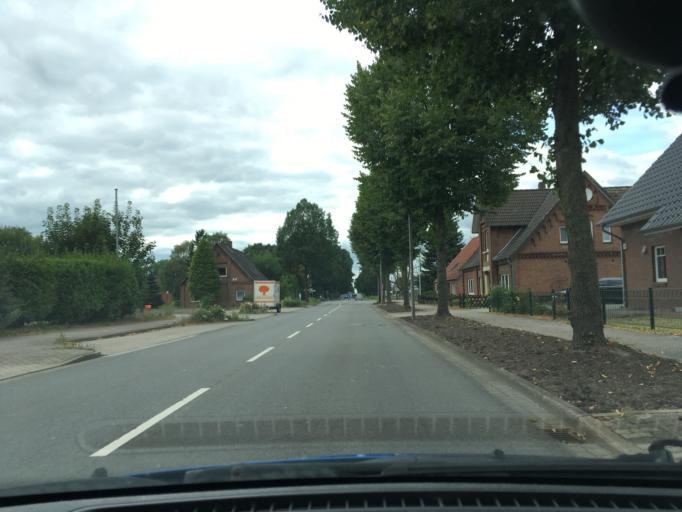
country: DE
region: Lower Saxony
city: Neu Wulmstorf
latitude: 53.4272
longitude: 9.7839
